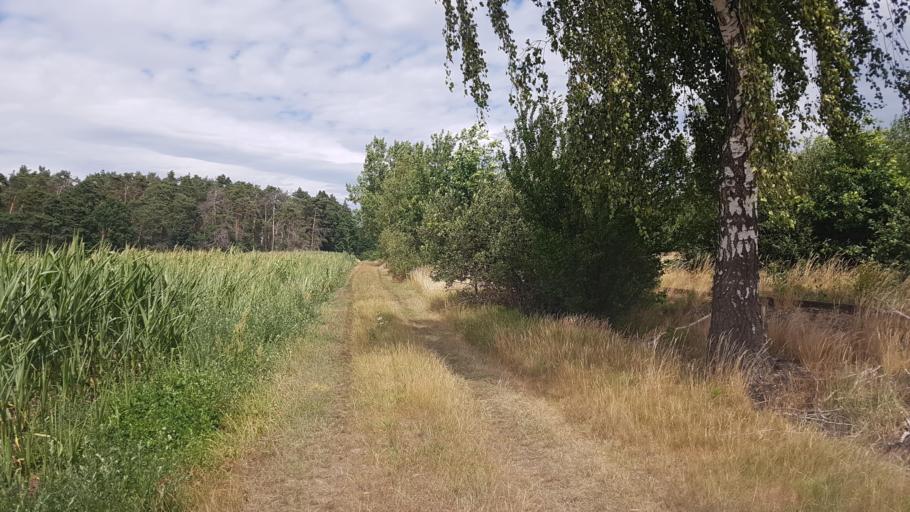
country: DE
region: Brandenburg
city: Finsterwalde
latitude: 51.6623
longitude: 13.7041
